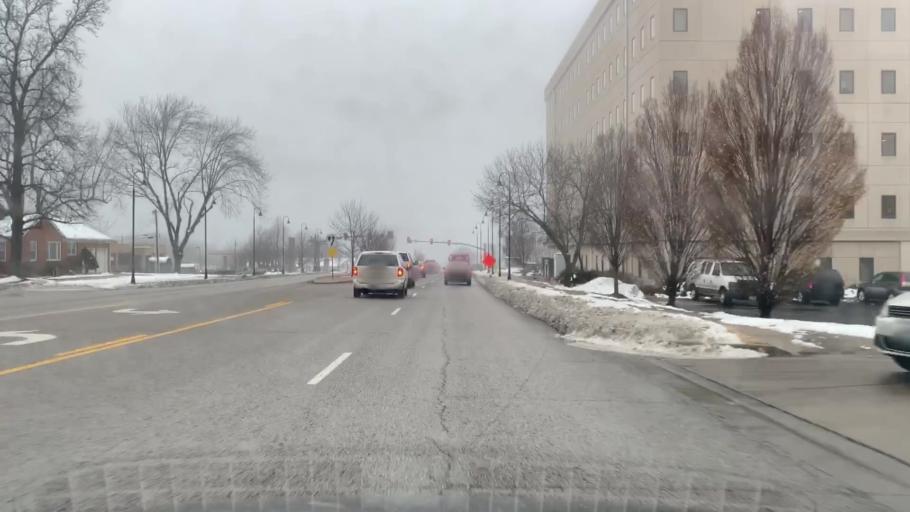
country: US
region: Missouri
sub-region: Jackson County
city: Raytown
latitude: 39.0096
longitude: -94.4802
